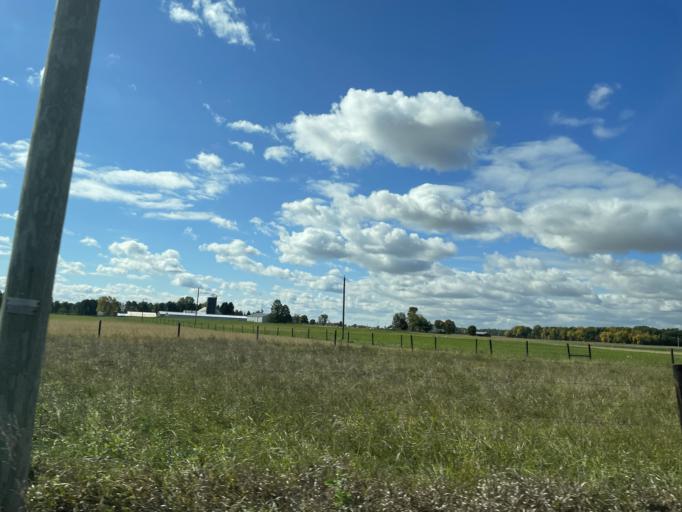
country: US
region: Indiana
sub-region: Whitley County
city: Churubusco
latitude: 41.1240
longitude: -85.2814
